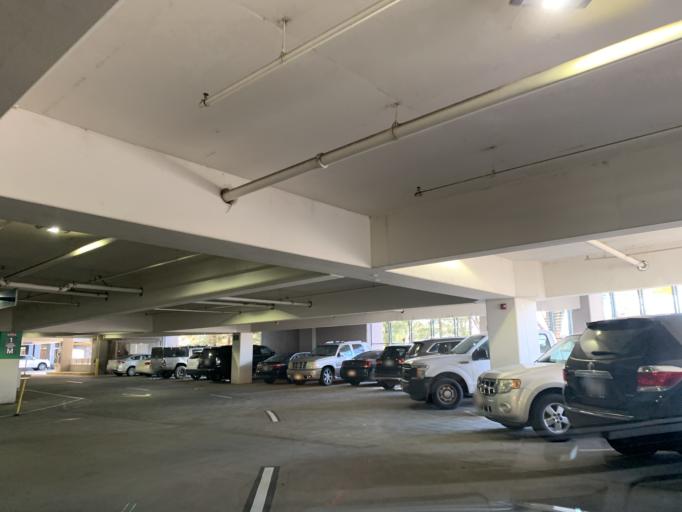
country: US
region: California
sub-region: Yolo County
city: West Sacramento
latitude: 38.6950
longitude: -121.5915
